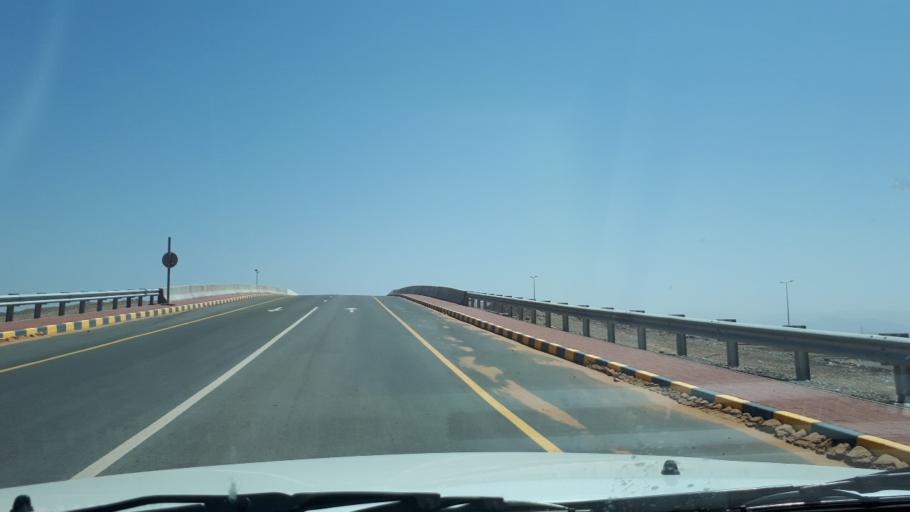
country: OM
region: Ash Sharqiyah
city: Al Qabil
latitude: 22.5226
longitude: 58.7404
